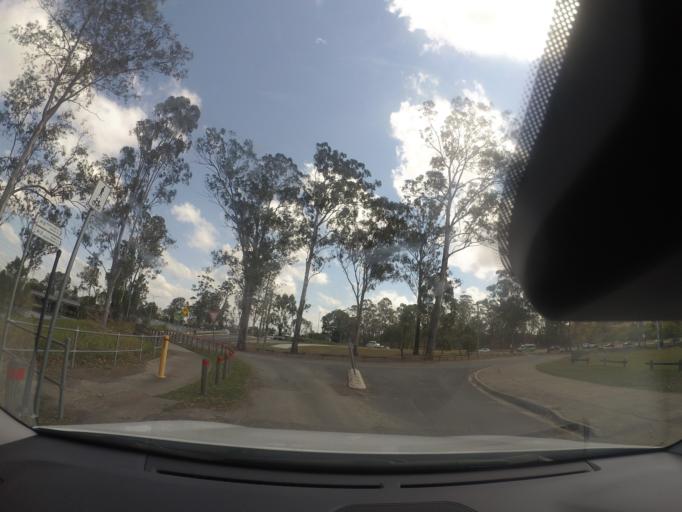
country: AU
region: Queensland
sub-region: Logan
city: Logan City
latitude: -27.6636
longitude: 153.1202
